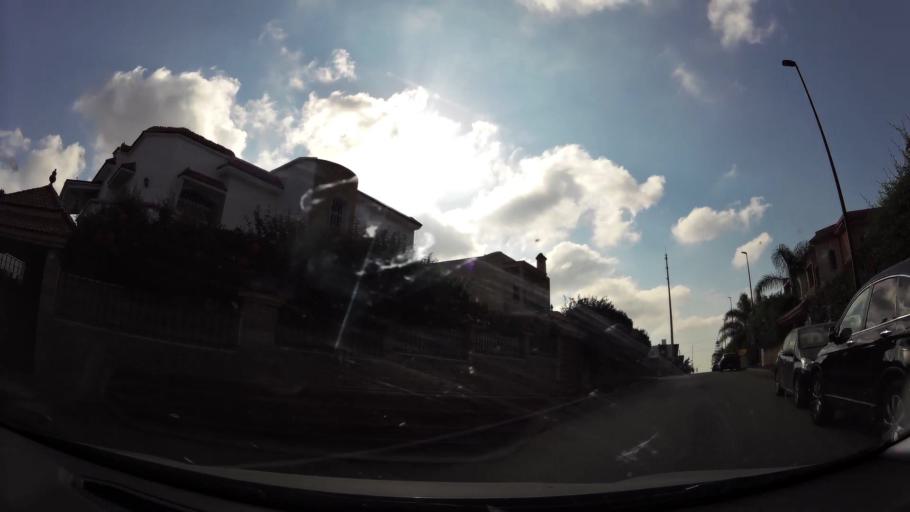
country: MA
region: Rabat-Sale-Zemmour-Zaer
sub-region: Skhirate-Temara
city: Temara
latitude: 33.9502
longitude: -6.8663
